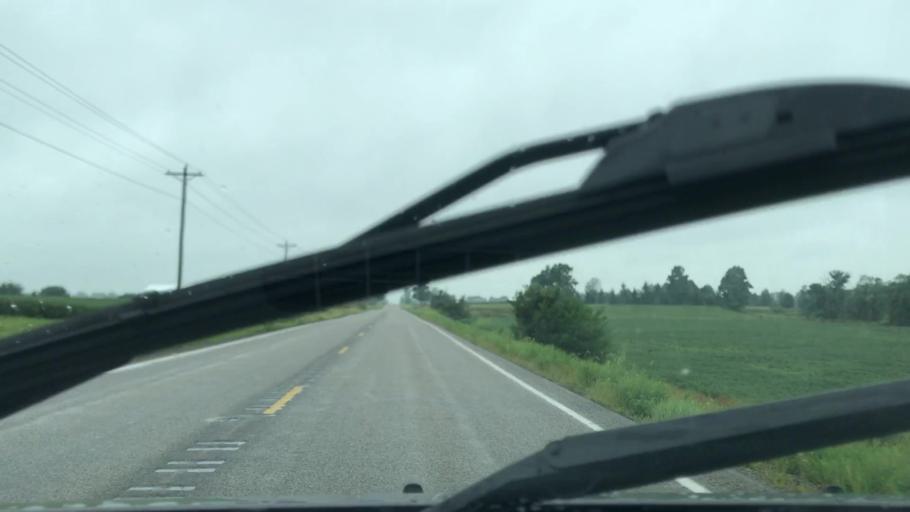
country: US
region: Indiana
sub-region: Boone County
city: Lebanon
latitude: 40.1264
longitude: -86.4367
